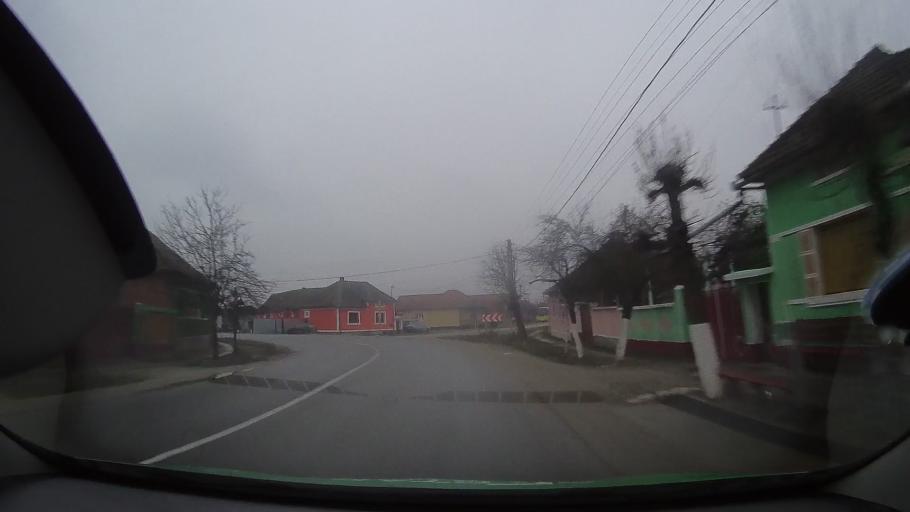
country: RO
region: Bihor
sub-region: Comuna Tulca
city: Tulca
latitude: 46.7901
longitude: 21.8190
